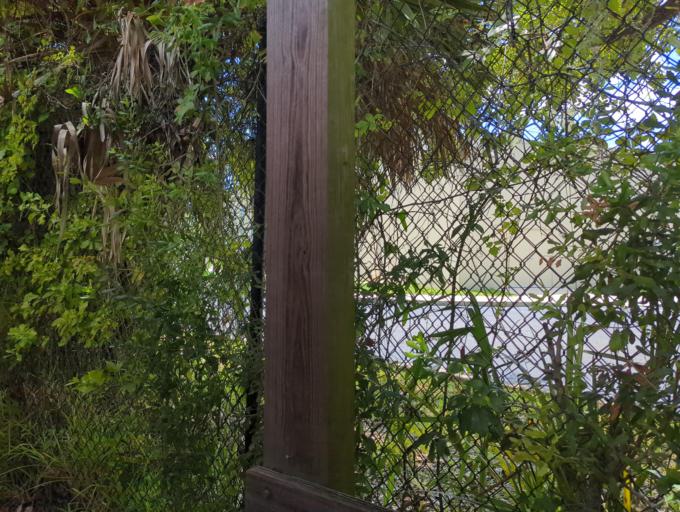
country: US
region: Florida
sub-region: Duval County
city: Jacksonville
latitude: 30.4014
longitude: -81.6461
